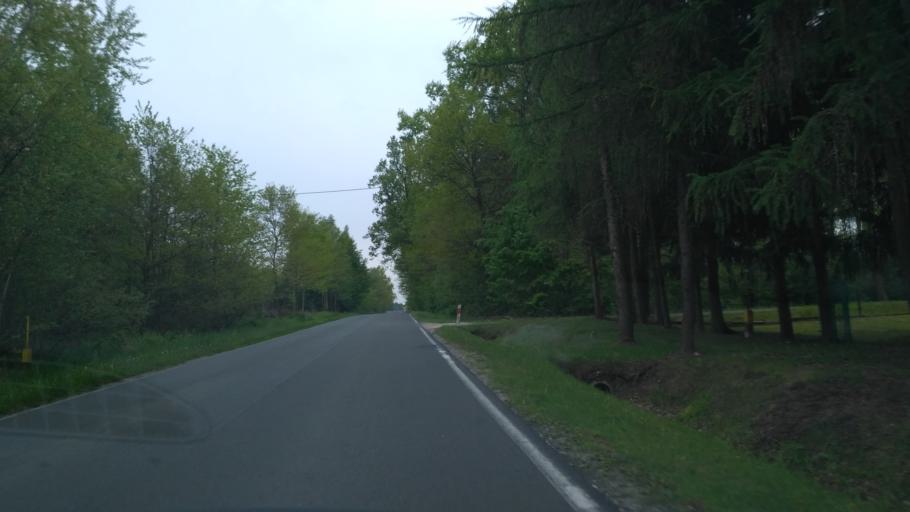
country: PL
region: Subcarpathian Voivodeship
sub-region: Powiat ropczycko-sedziszowski
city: Sedziszow Malopolski
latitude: 50.1299
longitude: 21.7540
